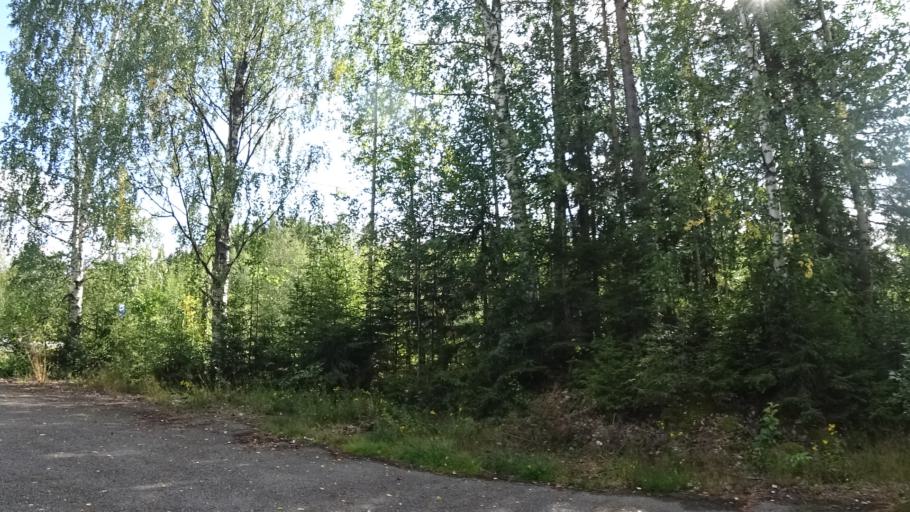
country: RU
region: Republic of Karelia
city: Vyartsilya
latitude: 62.2576
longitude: 30.7538
